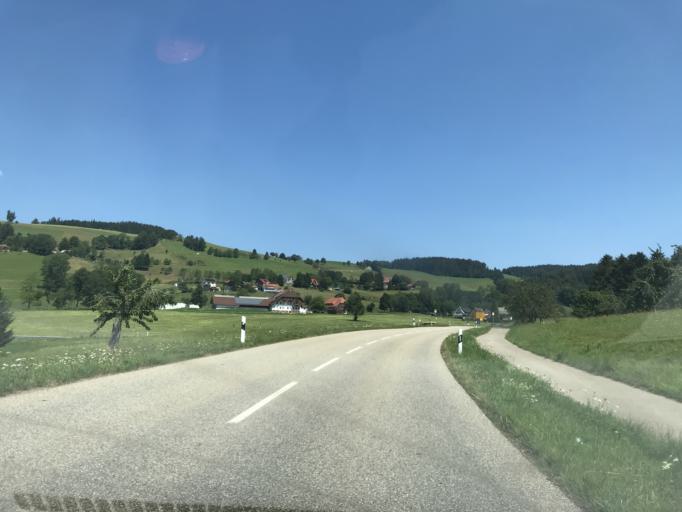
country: DE
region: Baden-Wuerttemberg
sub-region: Freiburg Region
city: Sankt Peter
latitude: 48.0187
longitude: 8.0431
